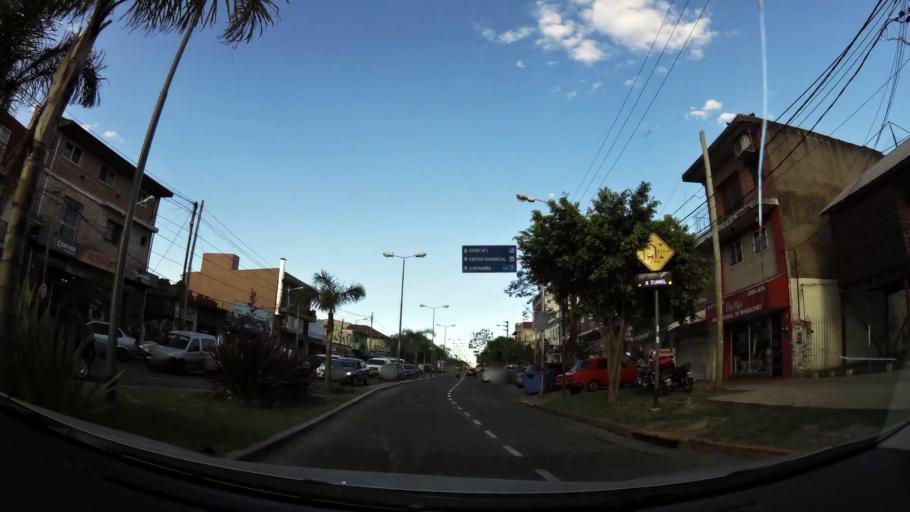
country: AR
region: Buenos Aires
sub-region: Partido de Tigre
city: Tigre
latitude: -34.4602
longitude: -58.5711
